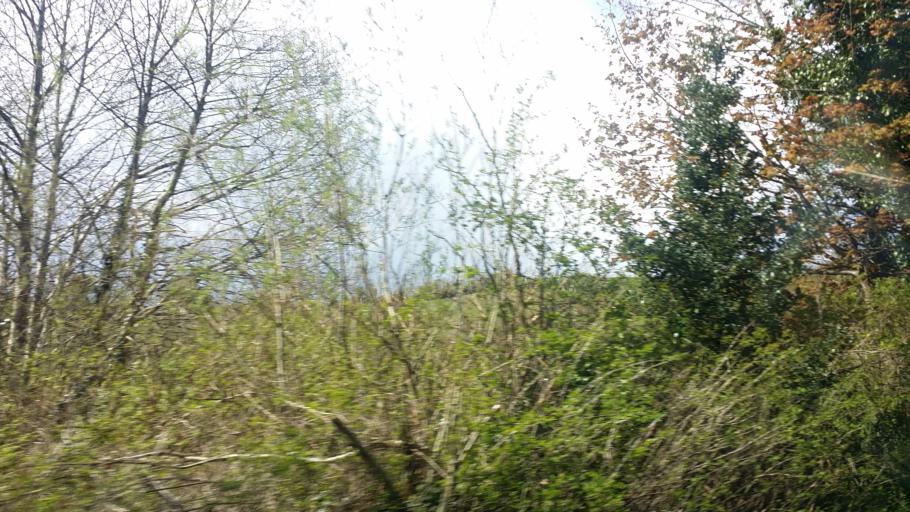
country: GB
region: Northern Ireland
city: Irvinestown
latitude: 54.4412
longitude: -7.7939
